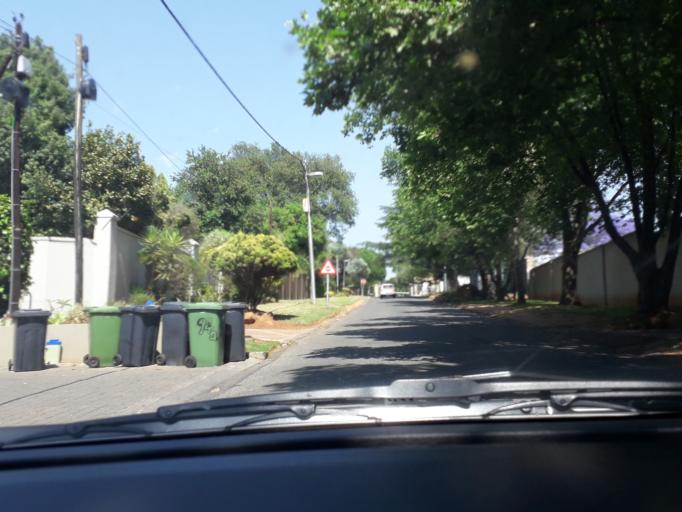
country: ZA
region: Gauteng
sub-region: City of Johannesburg Metropolitan Municipality
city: Johannesburg
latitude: -26.1228
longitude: 28.0641
